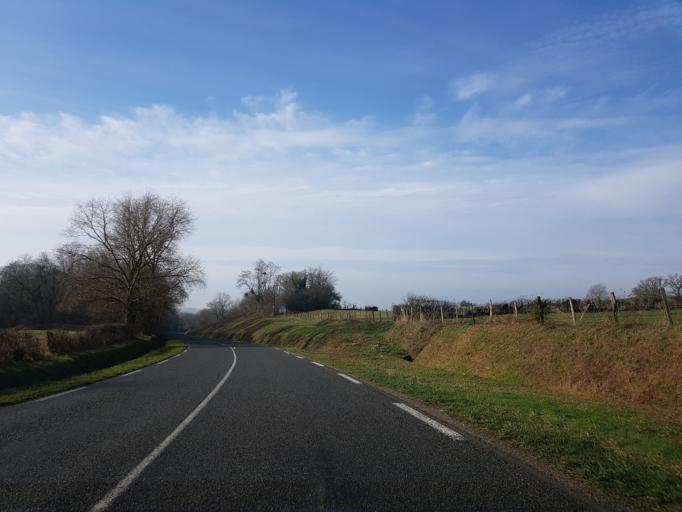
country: FR
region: Bourgogne
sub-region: Departement de Saone-et-Loire
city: La Motte-Saint-Jean
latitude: 46.5966
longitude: 3.9529
